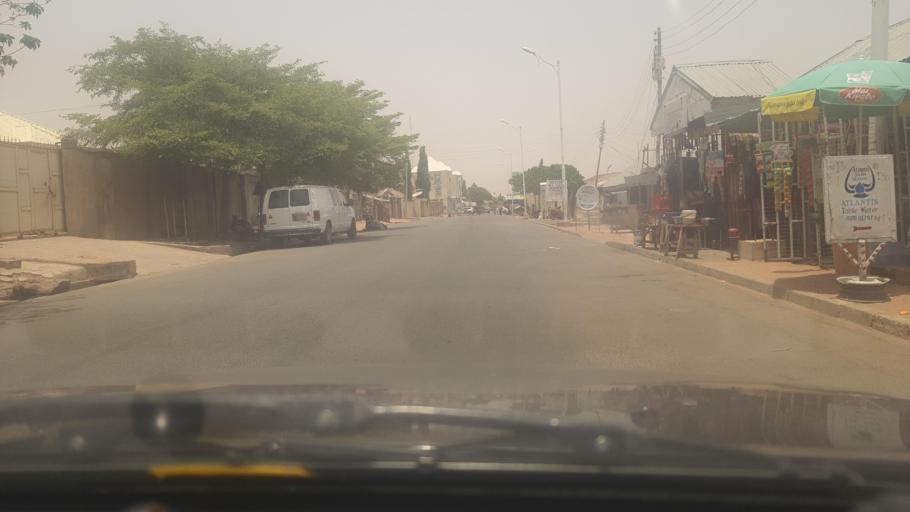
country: NG
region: Gombe
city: Gombe
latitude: 10.3013
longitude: 11.1467
